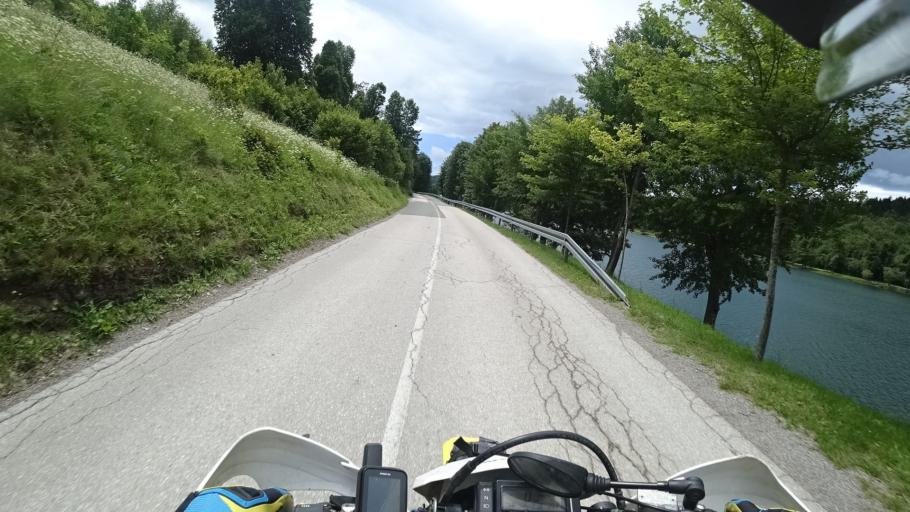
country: HR
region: Primorsko-Goranska
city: Hreljin
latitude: 45.3101
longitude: 14.7160
